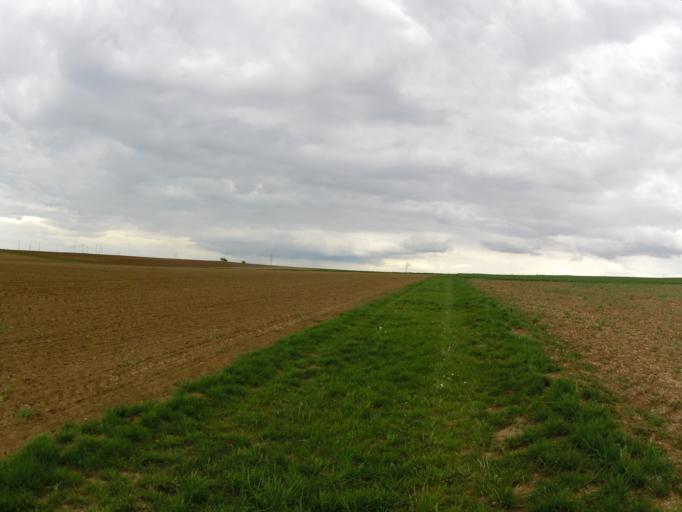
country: DE
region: Bavaria
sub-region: Regierungsbezirk Unterfranken
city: Oberpleichfeld
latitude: 49.8537
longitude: 10.0748
